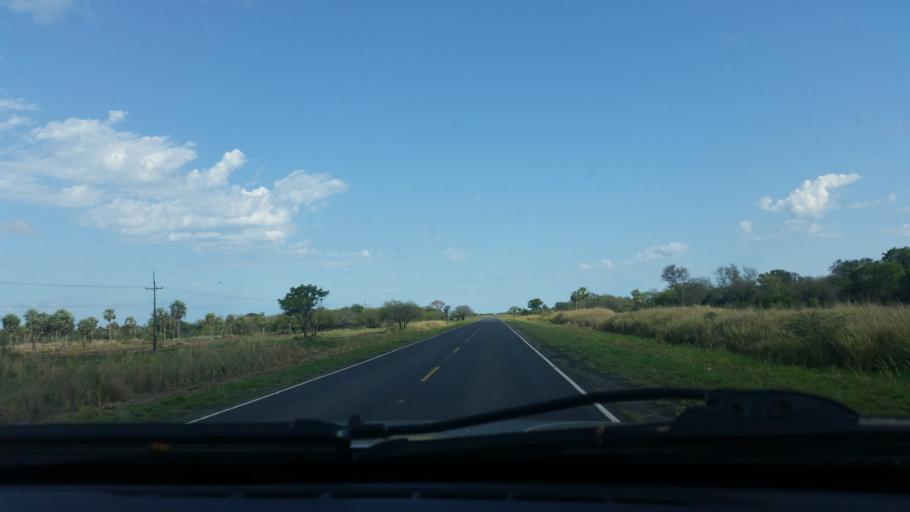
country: PY
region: Presidente Hayes
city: Benjamin Aceval
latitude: -24.9004
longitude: -57.6562
